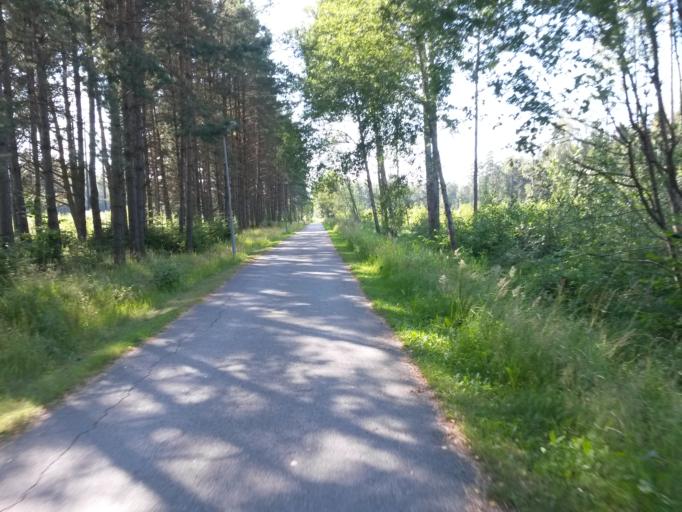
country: SE
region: Vaestra Goetaland
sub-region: Lidkopings Kommun
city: Lidkoping
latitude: 58.4947
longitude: 13.2074
